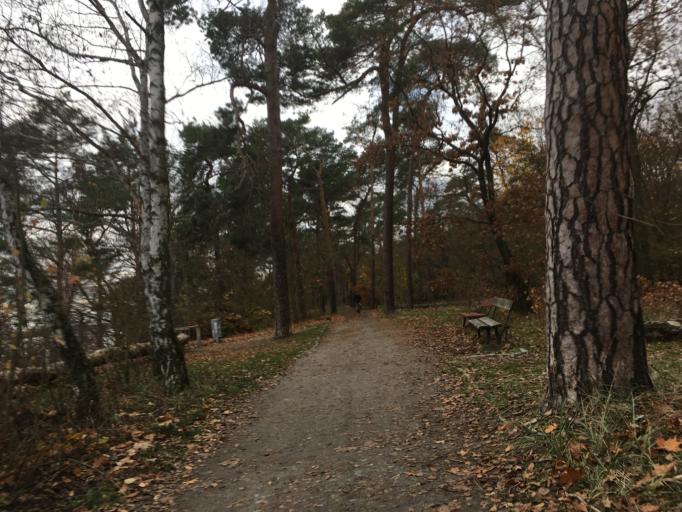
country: DE
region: Berlin
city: Rahnsdorf
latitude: 52.4476
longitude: 13.6627
